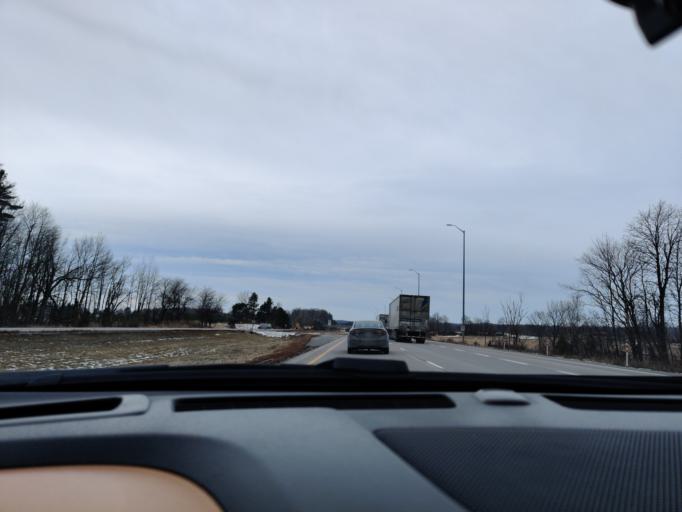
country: CA
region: Ontario
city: Gananoque
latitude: 44.3580
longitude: -76.0890
